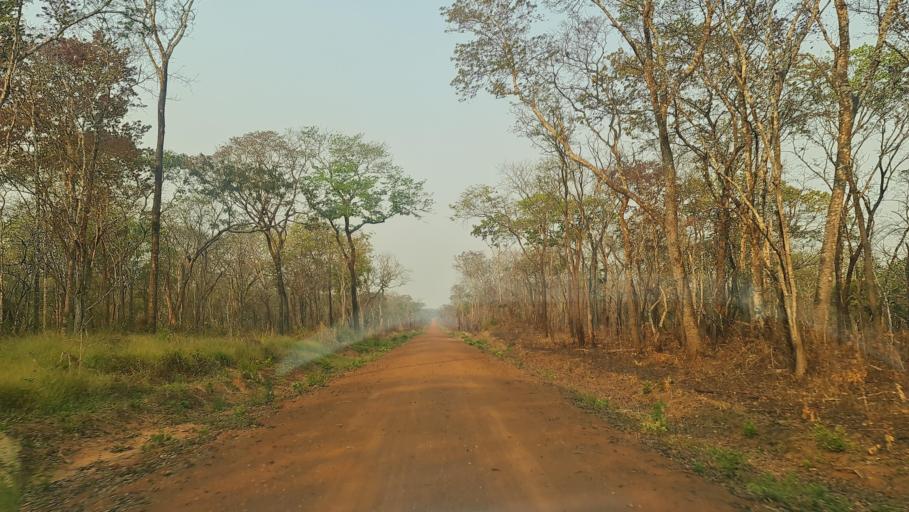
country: MZ
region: Zambezia
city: Quelimane
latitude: -17.1149
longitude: 37.1649
